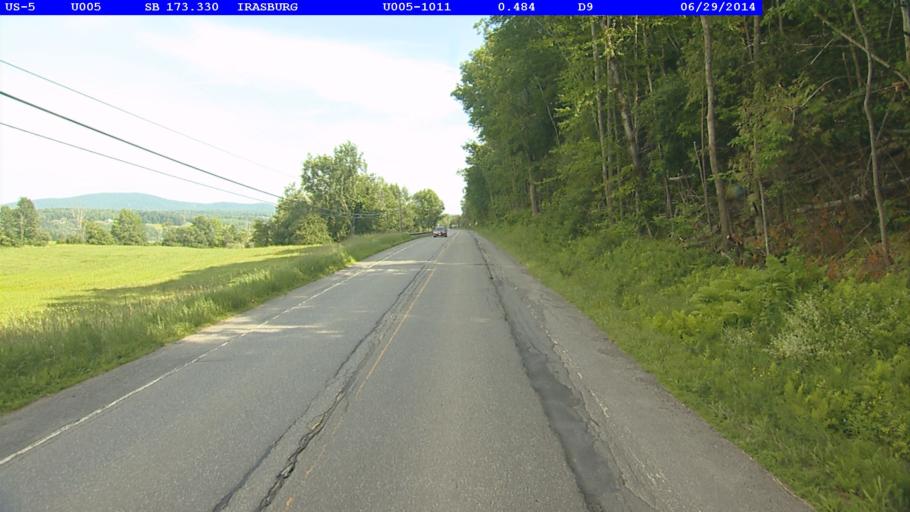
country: US
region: Vermont
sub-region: Orleans County
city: Newport
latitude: 44.8128
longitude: -72.2184
